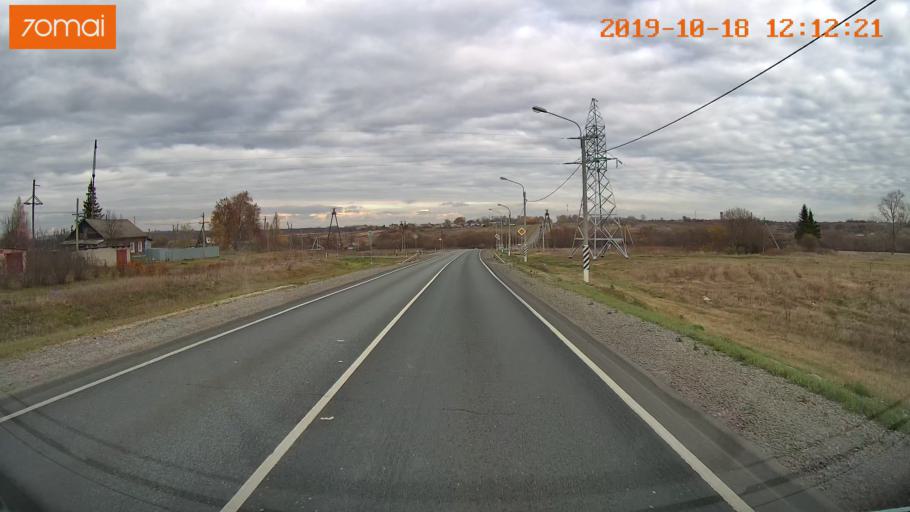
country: RU
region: Rjazan
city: Zakharovo
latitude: 54.4109
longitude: 39.3574
